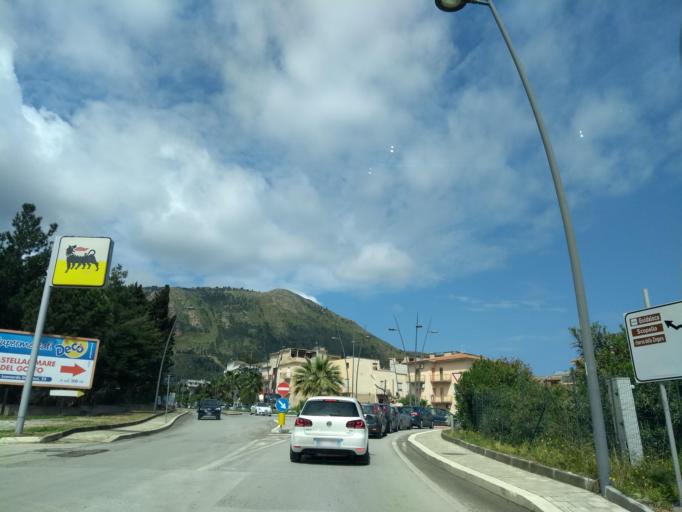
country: IT
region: Sicily
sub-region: Trapani
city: Castellammare del Golfo
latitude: 38.0169
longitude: 12.8892
